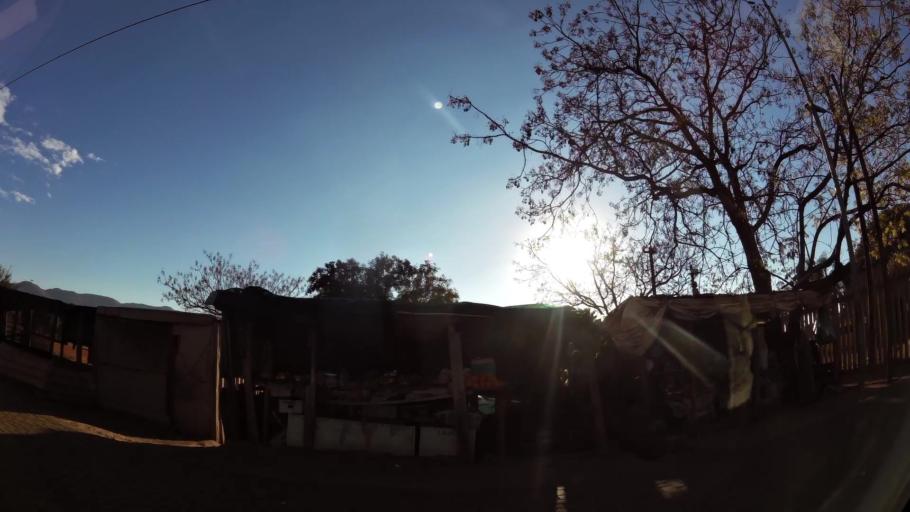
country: ZA
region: Limpopo
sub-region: Waterberg District Municipality
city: Mokopane
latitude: -24.1554
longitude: 28.9891
